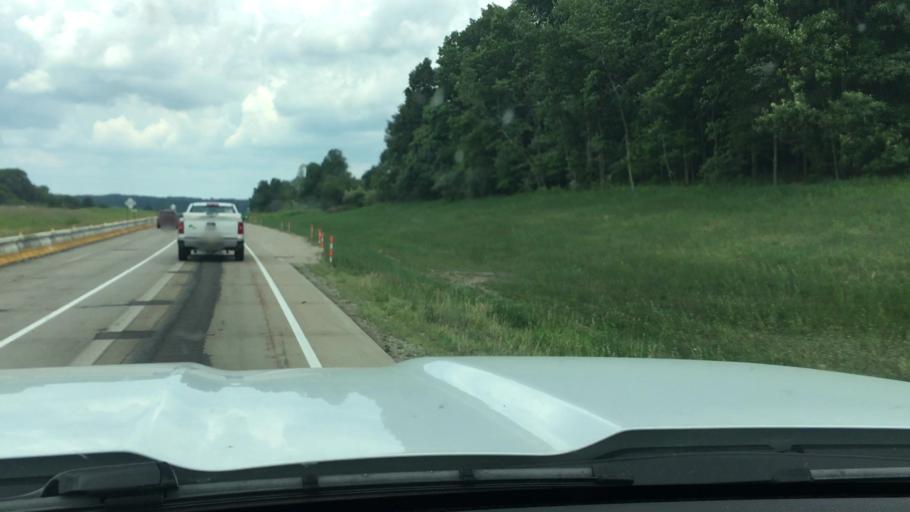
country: US
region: Michigan
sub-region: Kent County
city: Rockford
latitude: 43.1381
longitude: -85.5902
